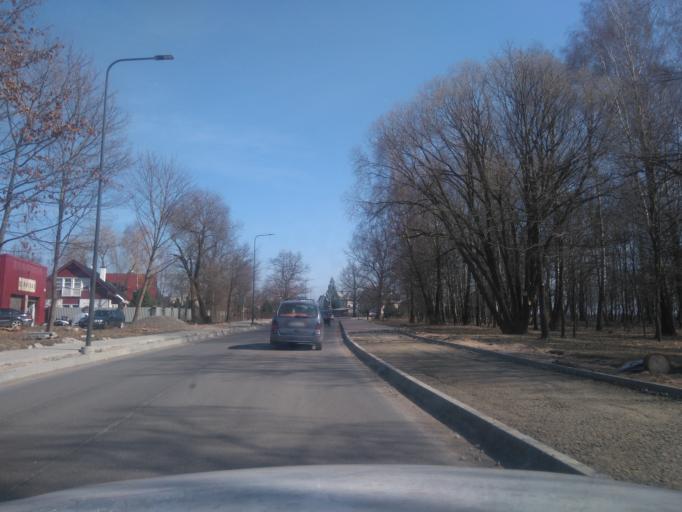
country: LT
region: Kauno apskritis
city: Dainava (Kaunas)
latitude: 54.8859
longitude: 23.9519
